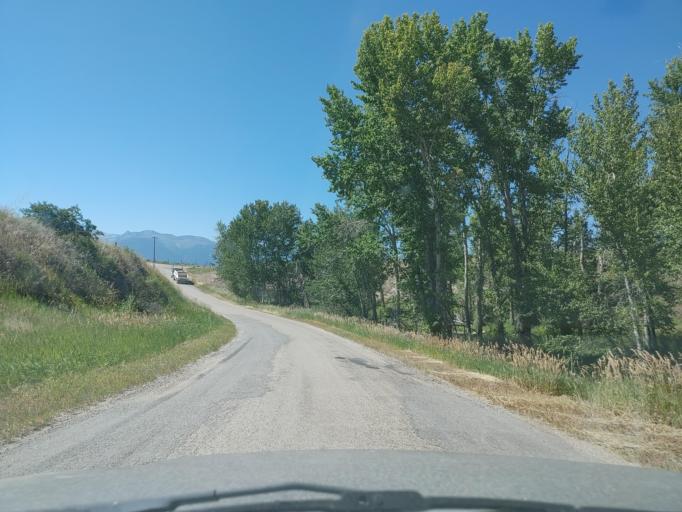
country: US
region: Montana
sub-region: Ravalli County
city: Hamilton
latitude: 46.3445
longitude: -114.0618
